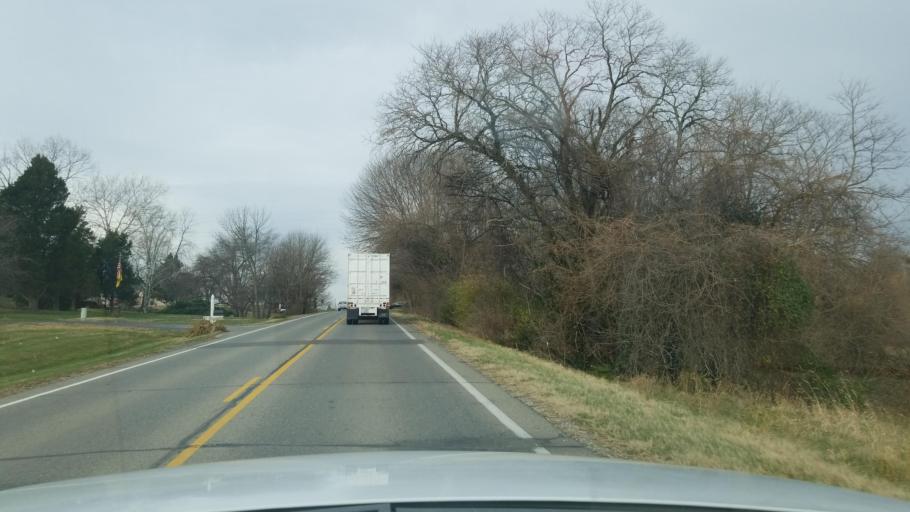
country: US
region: Indiana
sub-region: Posey County
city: Mount Vernon
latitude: 37.9291
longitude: -87.9333
